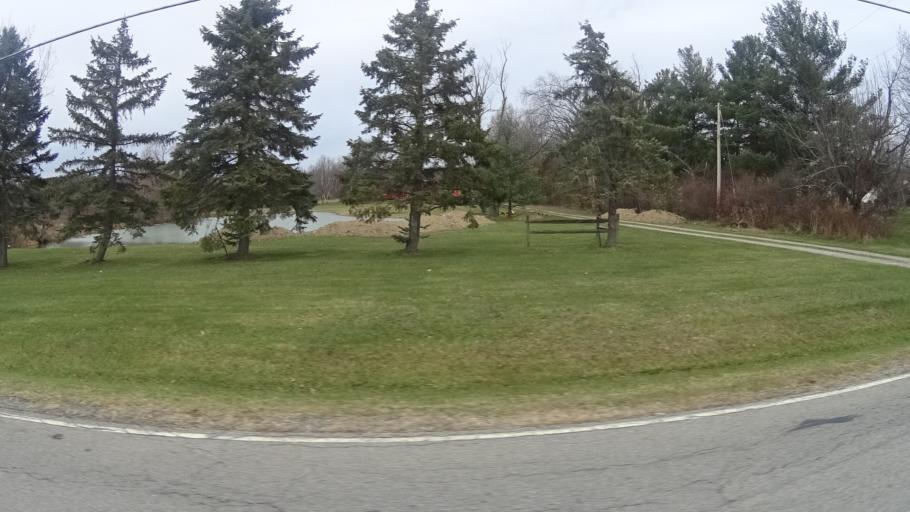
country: US
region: Ohio
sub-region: Cuyahoga County
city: Strongsville
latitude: 41.2894
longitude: -81.8884
